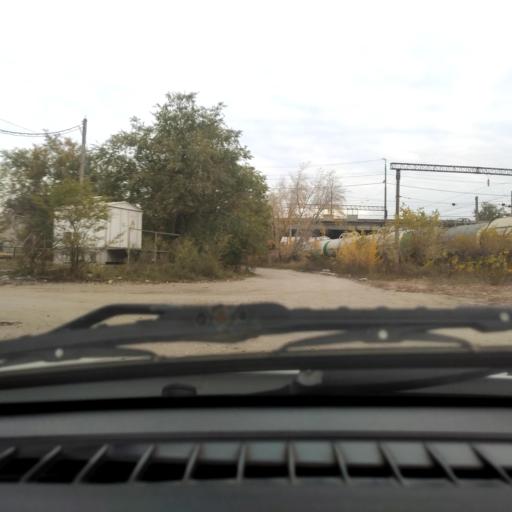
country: RU
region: Samara
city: Zhigulevsk
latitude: 53.4865
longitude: 49.4995
